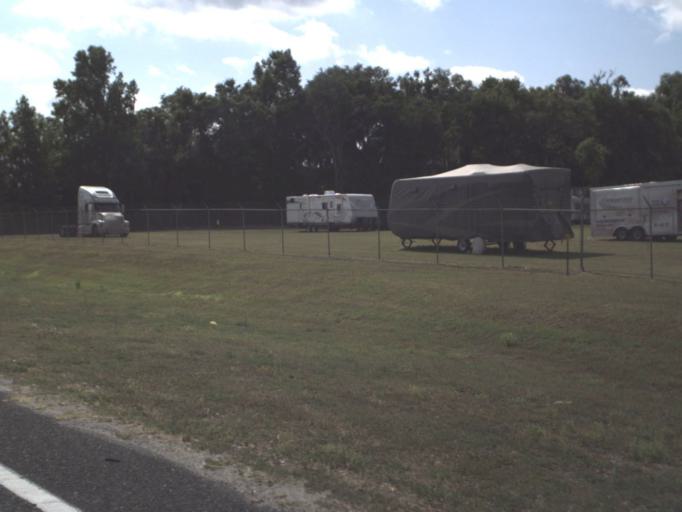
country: US
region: Florida
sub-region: Marion County
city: Ocala
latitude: 29.2668
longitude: -82.1779
